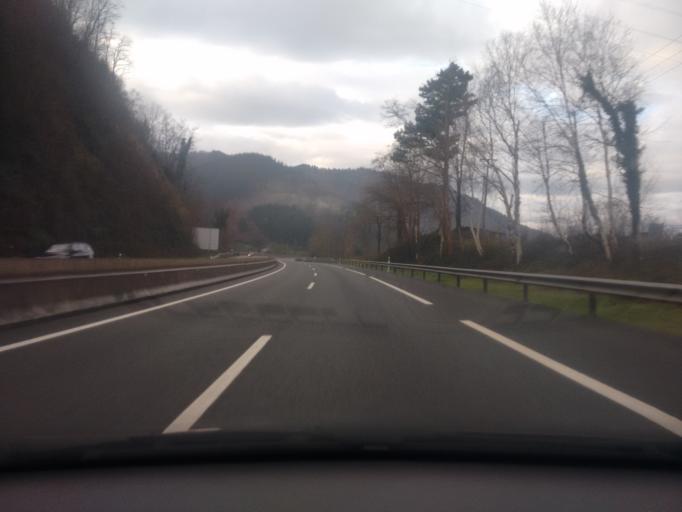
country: ES
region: Basque Country
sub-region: Provincia de Guipuzcoa
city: Eibar
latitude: 43.1870
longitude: -2.4603
